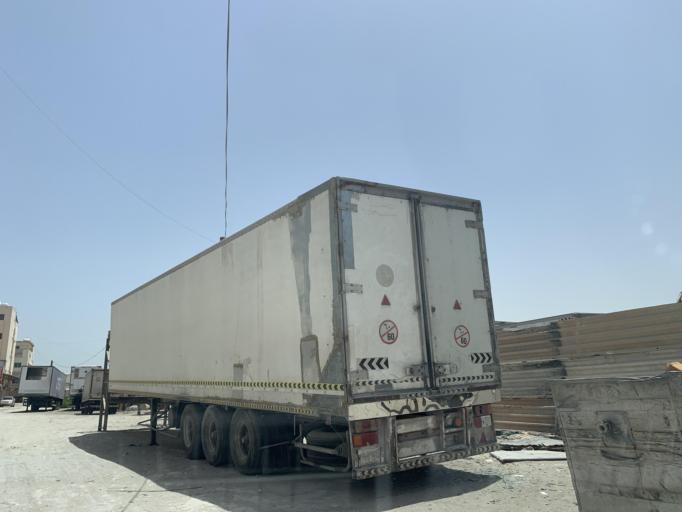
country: BH
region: Northern
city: Sitrah
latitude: 26.1758
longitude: 50.6077
